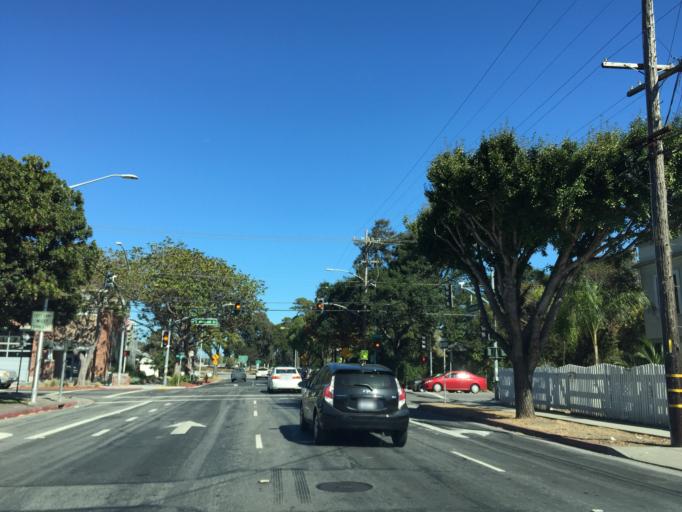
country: US
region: California
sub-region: San Mateo County
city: San Mateo
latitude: 37.5687
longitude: -122.3159
